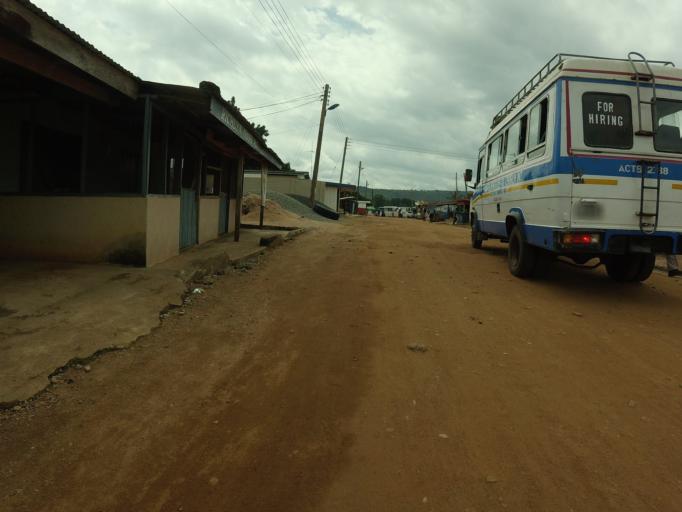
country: GH
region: Volta
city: Ho
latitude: 6.6024
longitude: 0.4691
